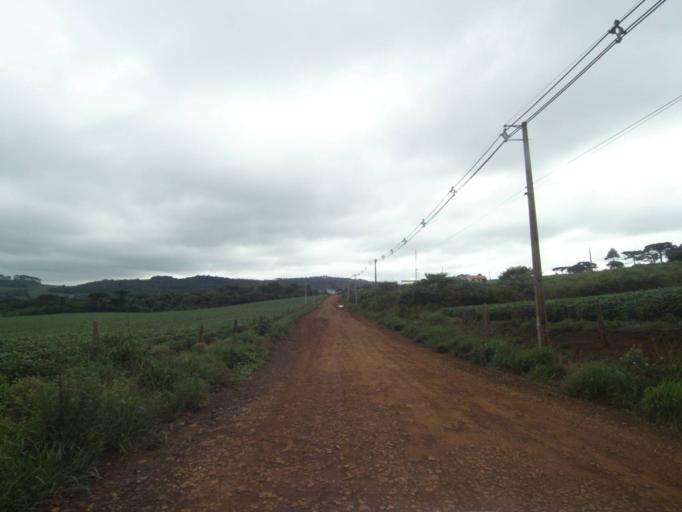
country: BR
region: Parana
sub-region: Pitanga
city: Pitanga
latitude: -24.9409
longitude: -51.8790
